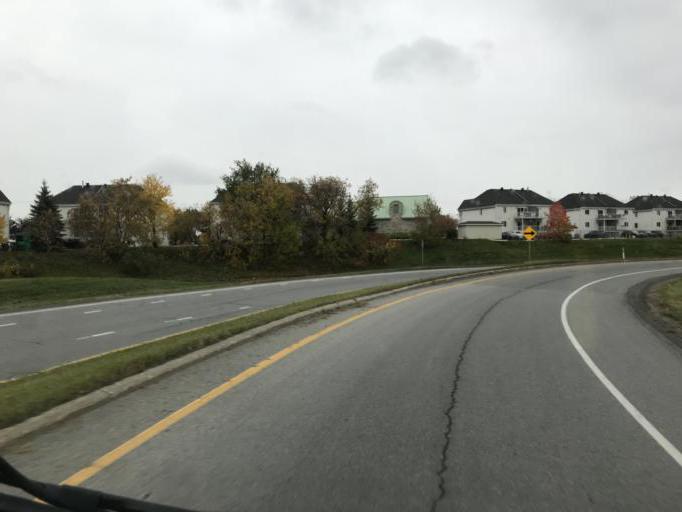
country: CA
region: Quebec
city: Bois-des-Filion
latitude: 45.6703
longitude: -73.7647
